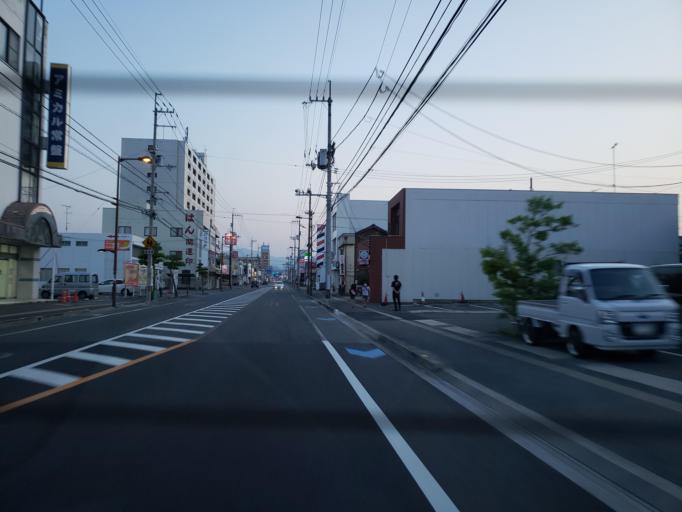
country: JP
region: Ehime
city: Hojo
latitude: 34.0547
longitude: 132.9873
